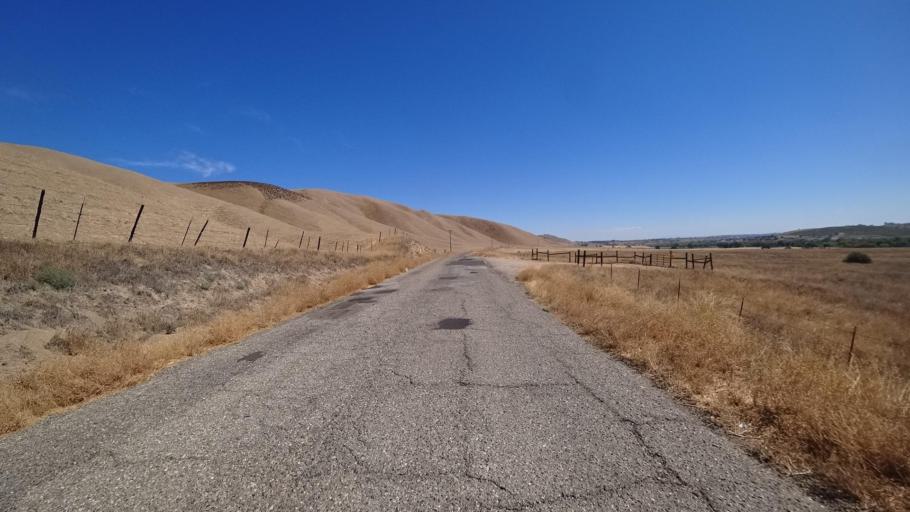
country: US
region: California
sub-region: San Luis Obispo County
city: San Miguel
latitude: 35.7846
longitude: -120.7121
